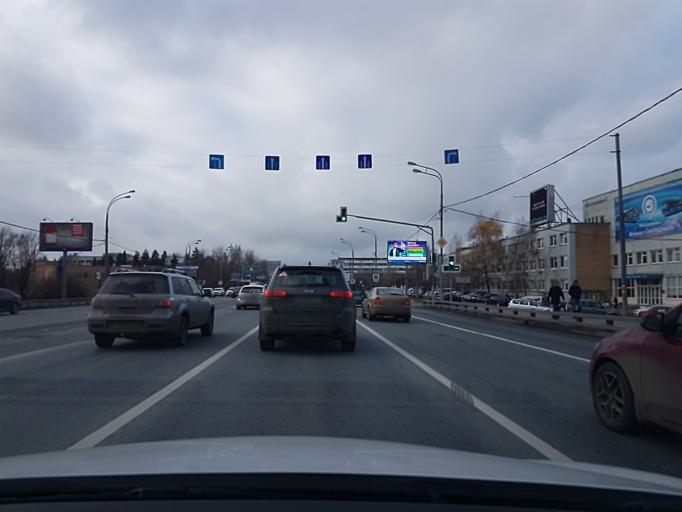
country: RU
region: Moscow
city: Strogino
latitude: 55.8279
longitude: 37.4193
